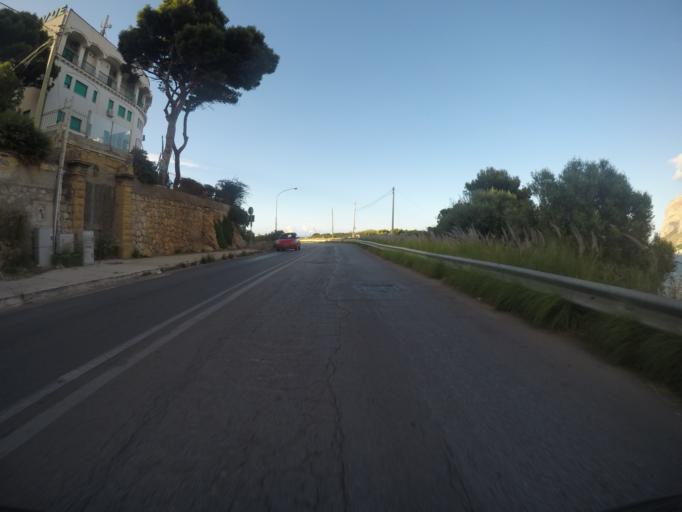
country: IT
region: Sicily
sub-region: Palermo
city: Isola delle Femmine
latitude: 38.2009
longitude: 13.2689
